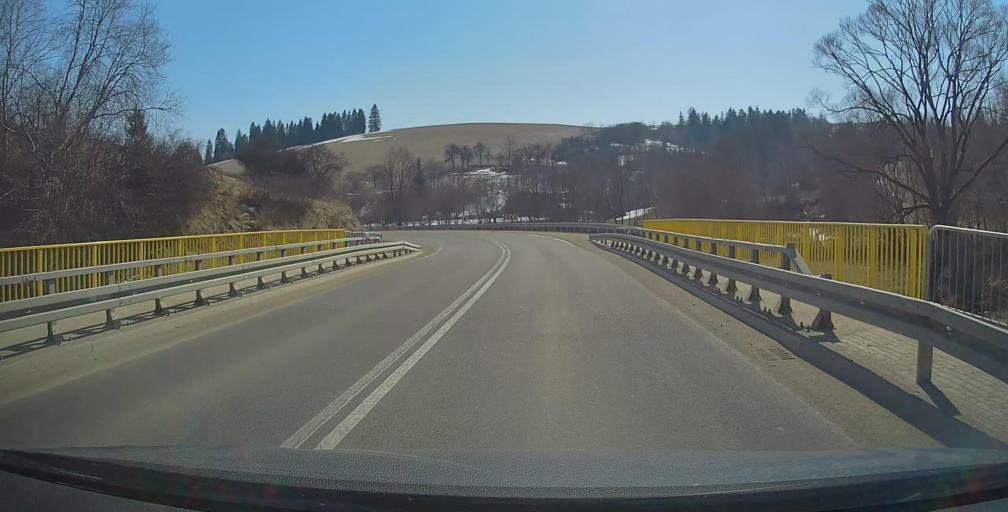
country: PL
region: Subcarpathian Voivodeship
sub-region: Powiat bieszczadzki
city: Ustrzyki Dolne
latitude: 49.4964
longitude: 22.6345
